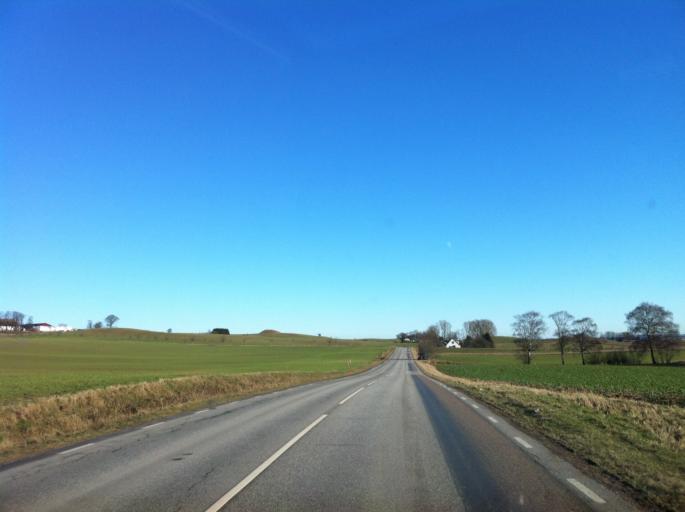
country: SE
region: Skane
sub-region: Svedala Kommun
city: Klagerup
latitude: 55.5772
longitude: 13.1945
